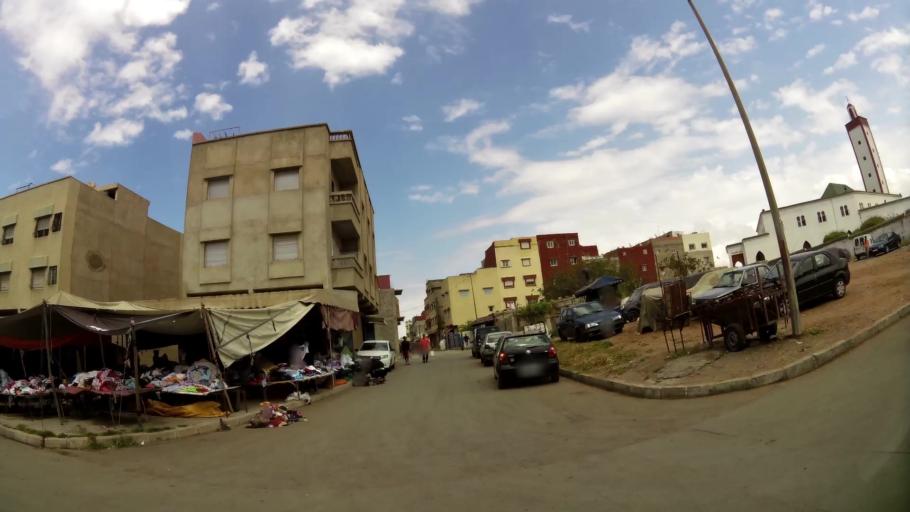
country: MA
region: Rabat-Sale-Zemmour-Zaer
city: Sale
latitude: 34.0546
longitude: -6.8192
